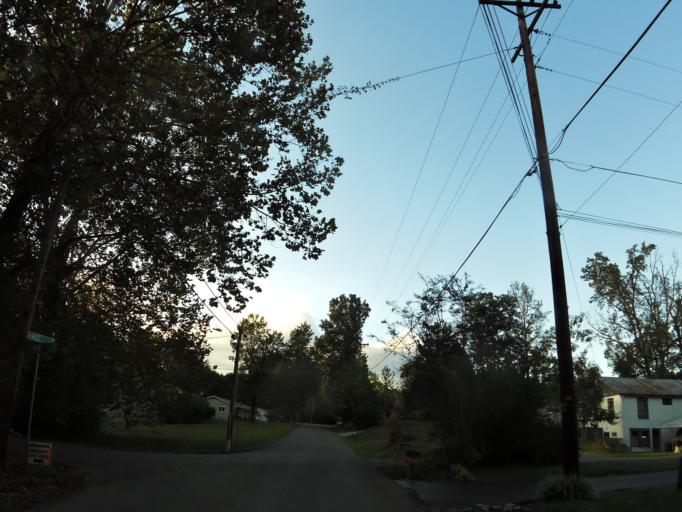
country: US
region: Tennessee
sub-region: Knox County
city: Knoxville
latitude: 35.9129
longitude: -83.9459
